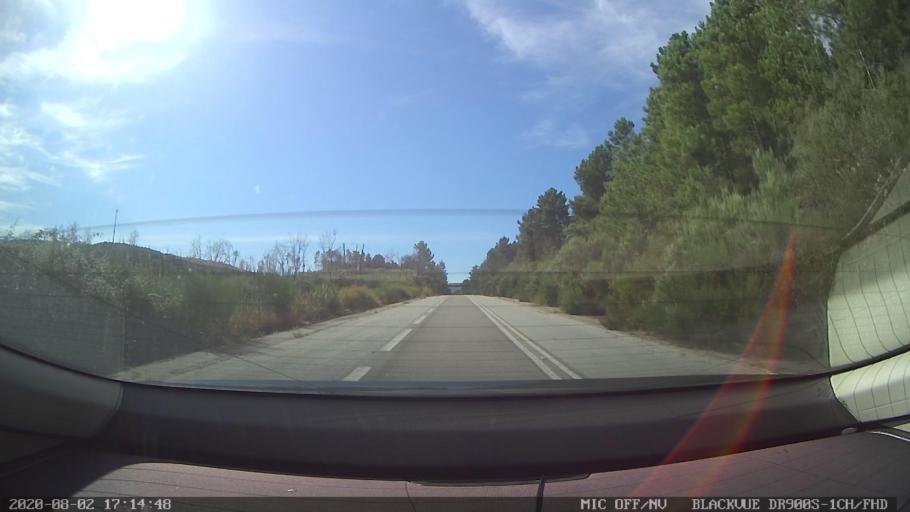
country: PT
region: Vila Real
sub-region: Sabrosa
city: Sabrosa
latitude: 41.3571
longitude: -7.5875
